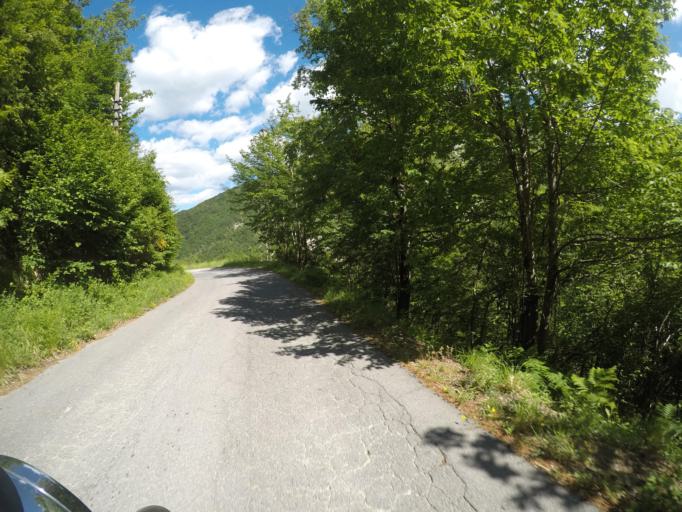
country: IT
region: Tuscany
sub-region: Provincia di Lucca
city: Minucciano
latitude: 44.1512
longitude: 10.1952
